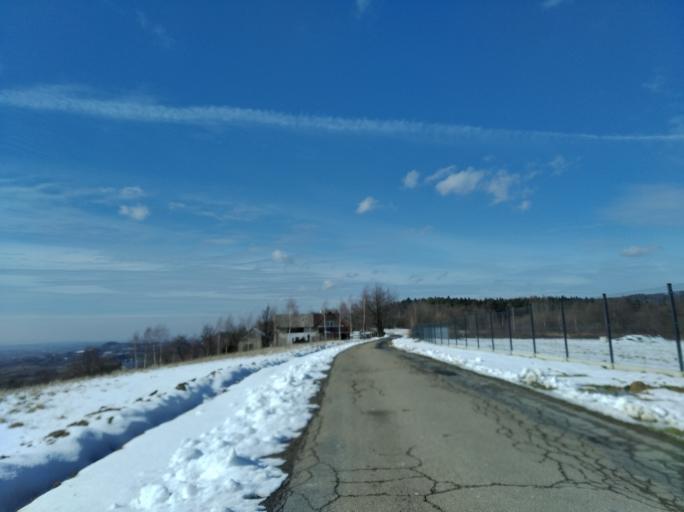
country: PL
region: Subcarpathian Voivodeship
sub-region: Powiat brzozowski
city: Jablonica Polska
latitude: 49.7306
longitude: 21.8642
